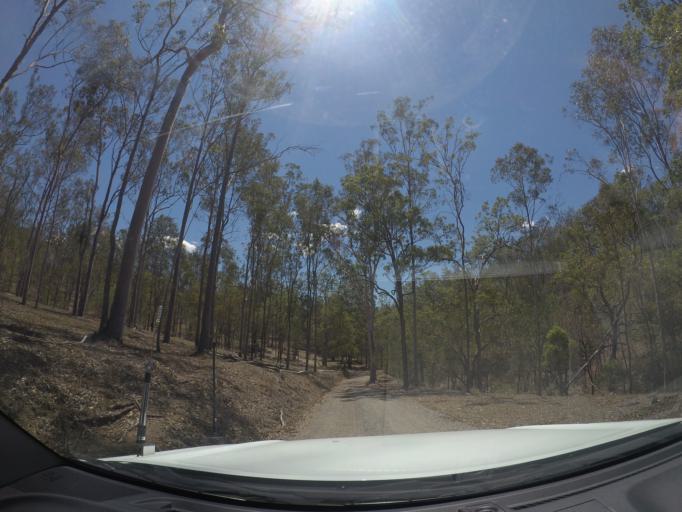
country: AU
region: Queensland
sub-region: Ipswich
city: Deebing Heights
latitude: -27.7672
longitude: 152.8113
